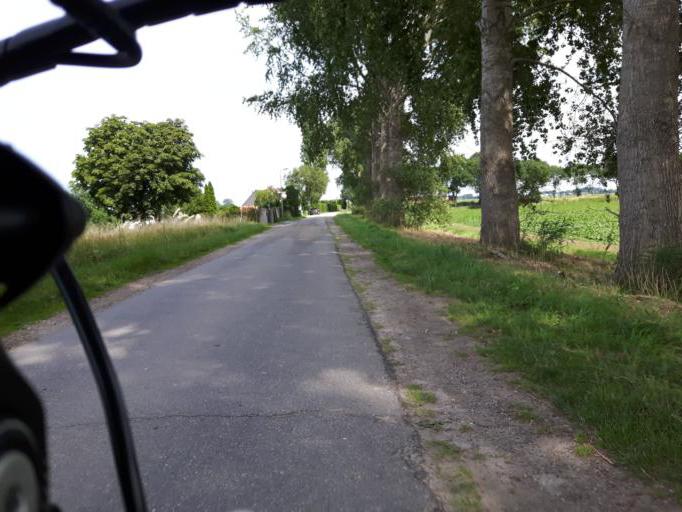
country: NL
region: North Brabant
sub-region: Gemeente Bergen op Zoom
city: Lepelstraat
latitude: 51.5889
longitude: 4.2741
